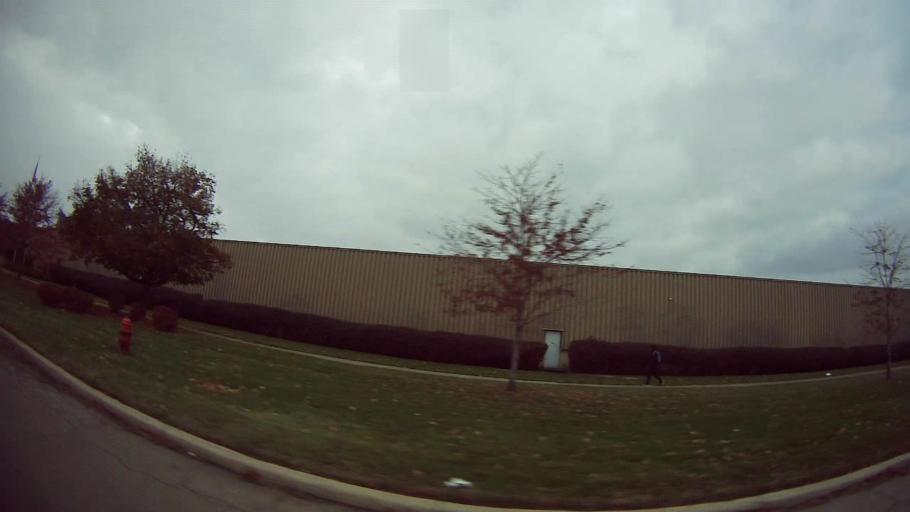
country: US
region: Michigan
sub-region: Macomb County
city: Warren
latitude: 42.4410
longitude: -83.0376
